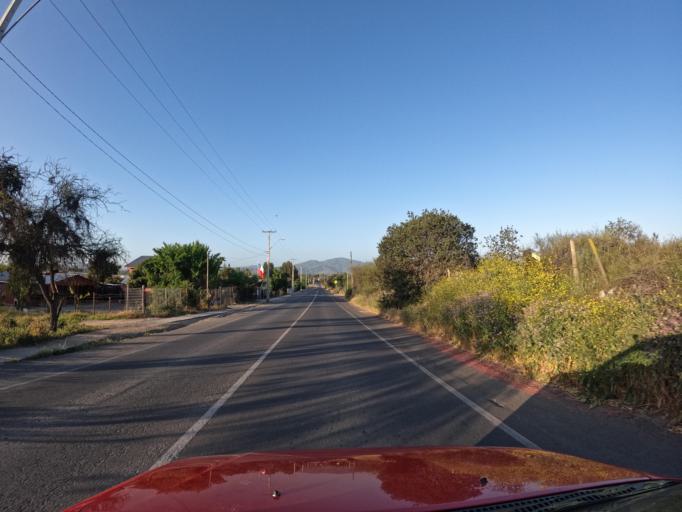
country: CL
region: O'Higgins
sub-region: Provincia de Colchagua
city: Santa Cruz
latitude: -34.3177
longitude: -71.3869
